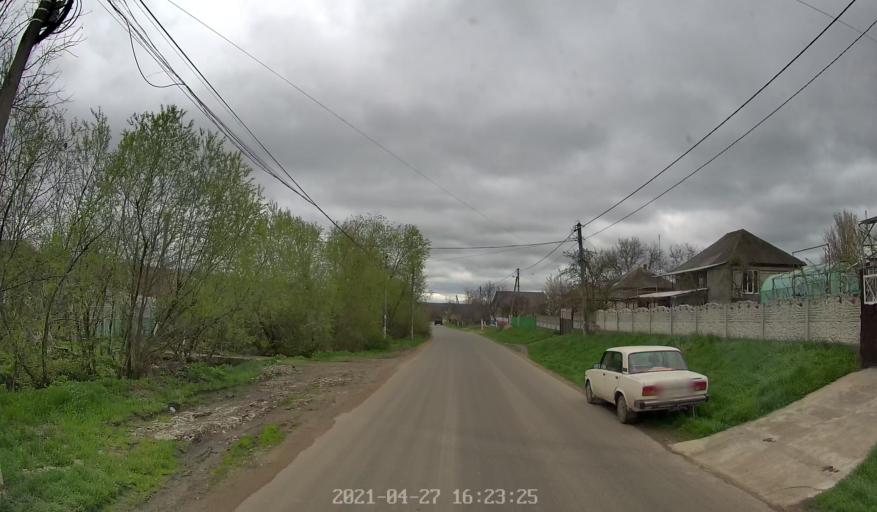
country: MD
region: Chisinau
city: Singera
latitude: 46.9989
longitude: 29.0176
